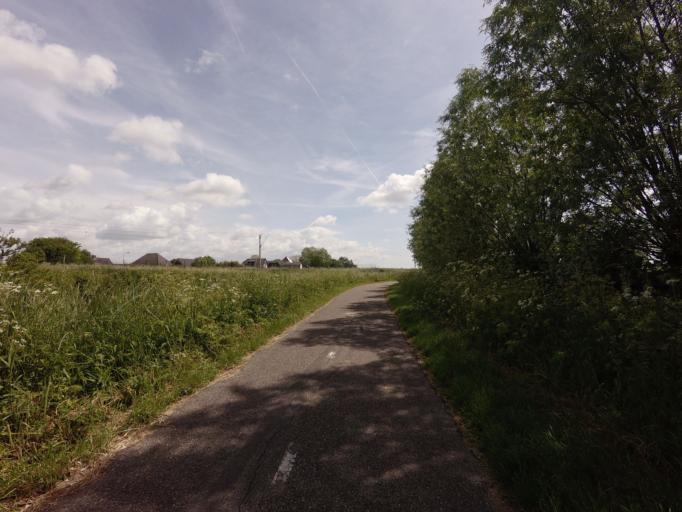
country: NL
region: North Holland
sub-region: Gemeente Hoorn
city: Hoorn
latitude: 52.6534
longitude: 5.0049
